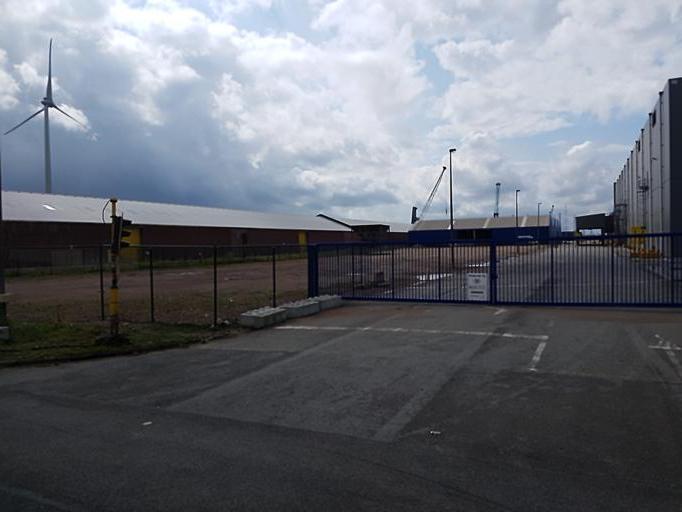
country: BE
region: Flanders
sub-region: Provincie Antwerpen
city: Antwerpen
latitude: 51.2594
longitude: 4.3886
